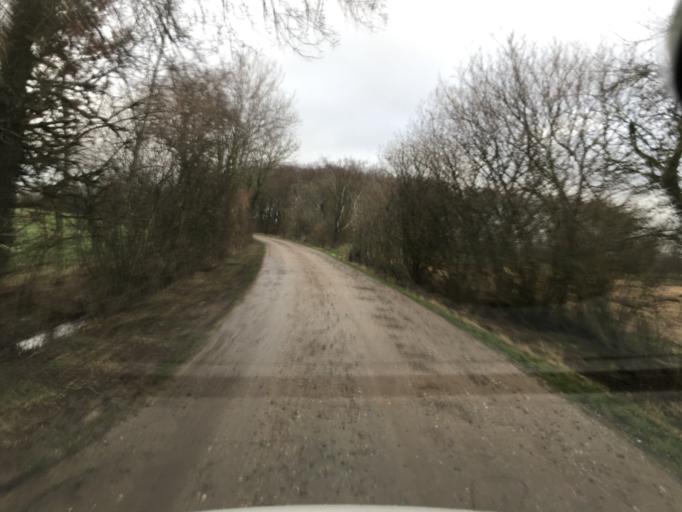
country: DE
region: Schleswig-Holstein
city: Bramstedtlund
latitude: 54.9523
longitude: 9.0471
